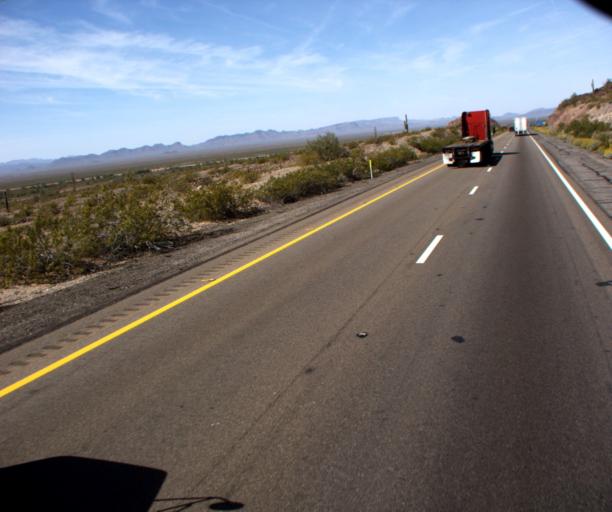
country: US
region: Arizona
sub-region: La Paz County
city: Salome
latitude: 33.6116
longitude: -113.6346
